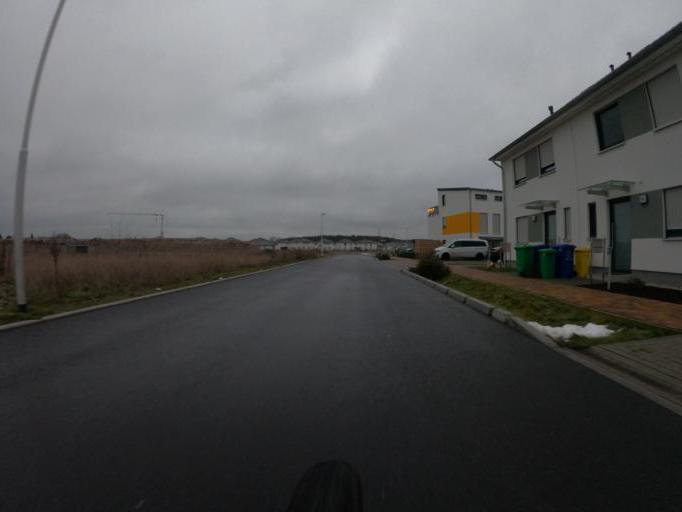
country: DE
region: Brandenburg
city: Schulzendorf
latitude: 52.3581
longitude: 13.5808
